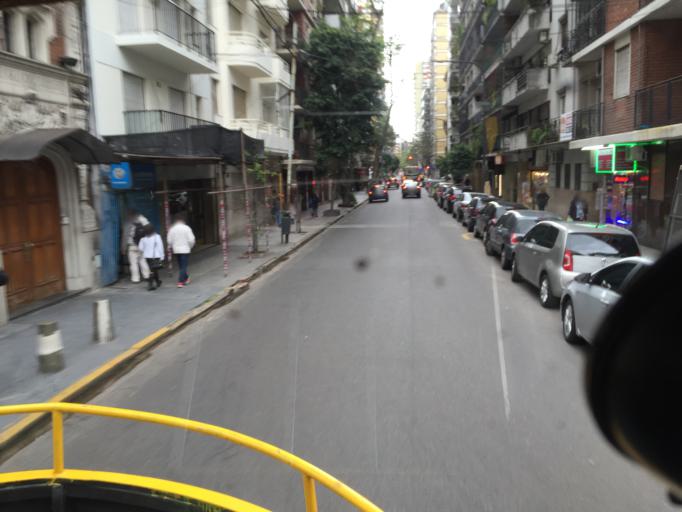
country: AR
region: Buenos Aires F.D.
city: Retiro
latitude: -34.5942
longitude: -58.4061
